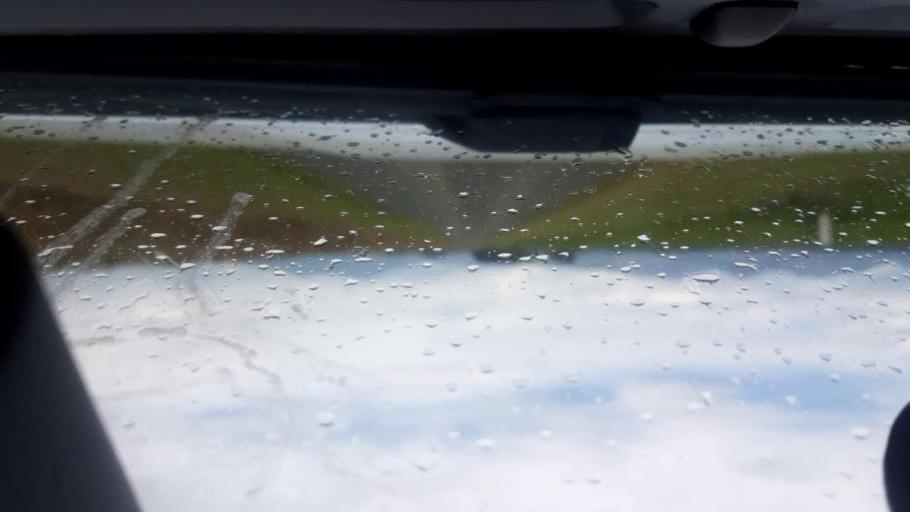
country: NZ
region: Canterbury
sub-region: Timaru District
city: Pleasant Point
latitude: -44.1177
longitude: 171.3583
